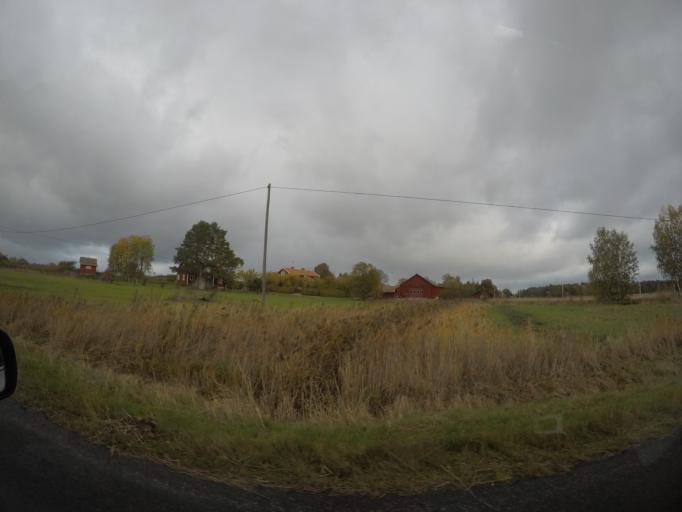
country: SE
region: Soedermanland
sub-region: Eskilstuna Kommun
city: Kvicksund
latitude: 59.3201
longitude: 16.3105
